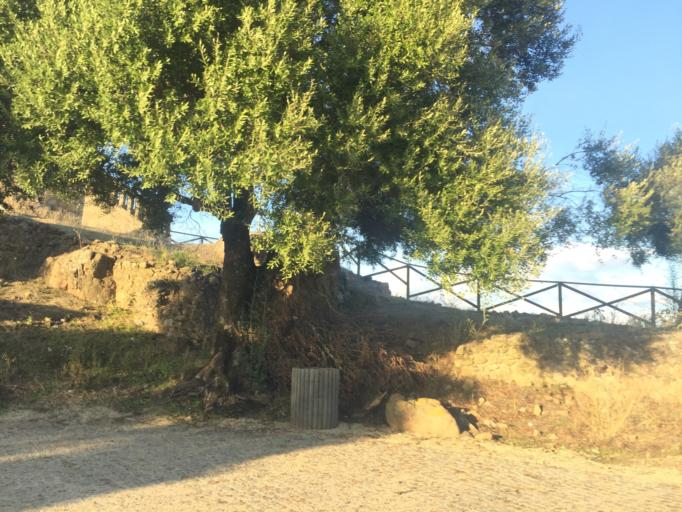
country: PT
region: Portalegre
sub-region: Alter do Chao
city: Alter do Chao
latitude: 39.1890
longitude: -7.6227
